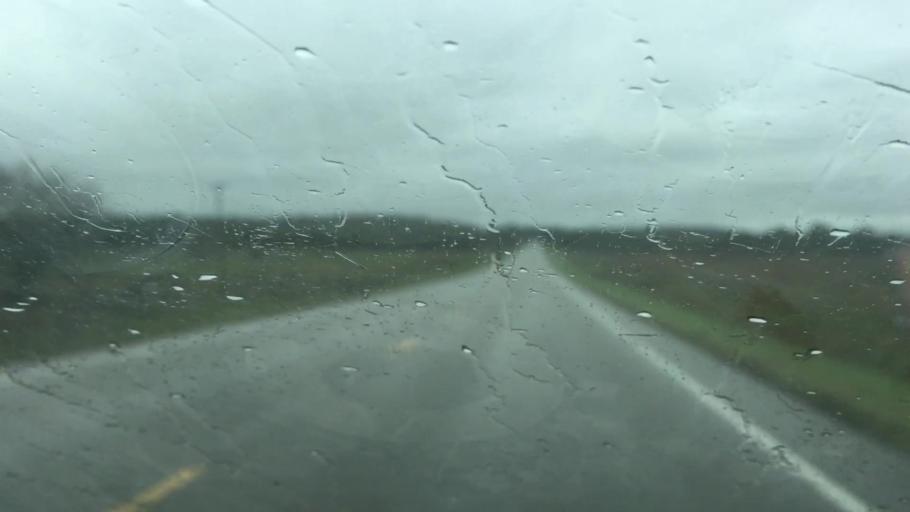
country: US
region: Kansas
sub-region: Anderson County
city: Garnett
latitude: 38.3792
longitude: -95.1130
